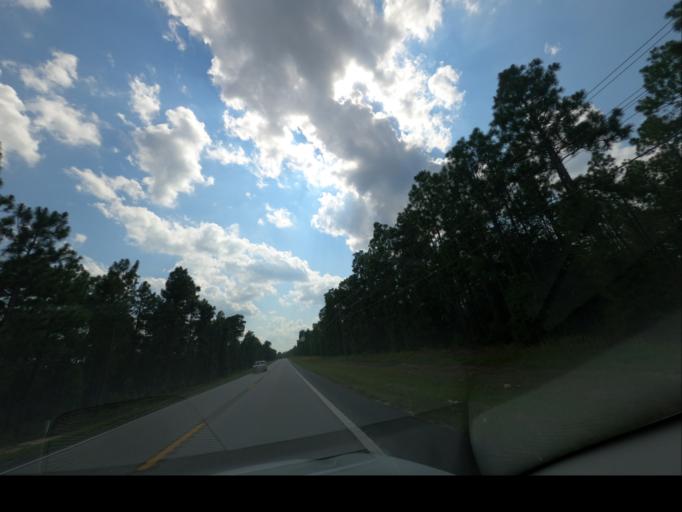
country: US
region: South Carolina
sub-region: Lexington County
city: South Congaree
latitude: 33.8672
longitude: -81.1949
